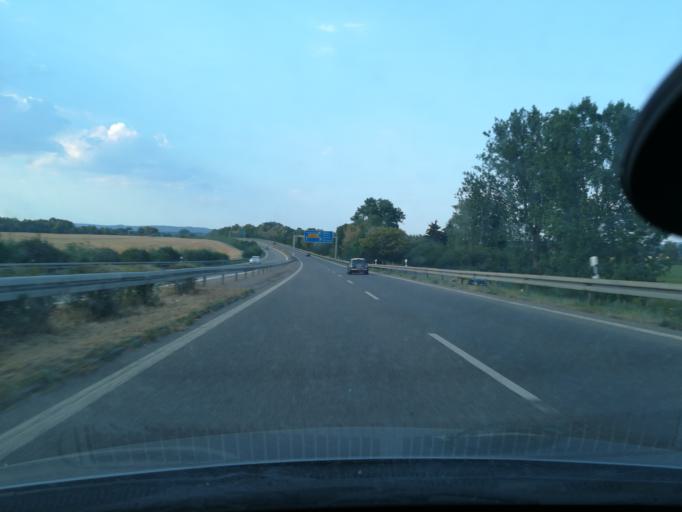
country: DE
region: Baden-Wuerttemberg
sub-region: Freiburg Region
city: Singen
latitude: 47.7849
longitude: 8.8279
